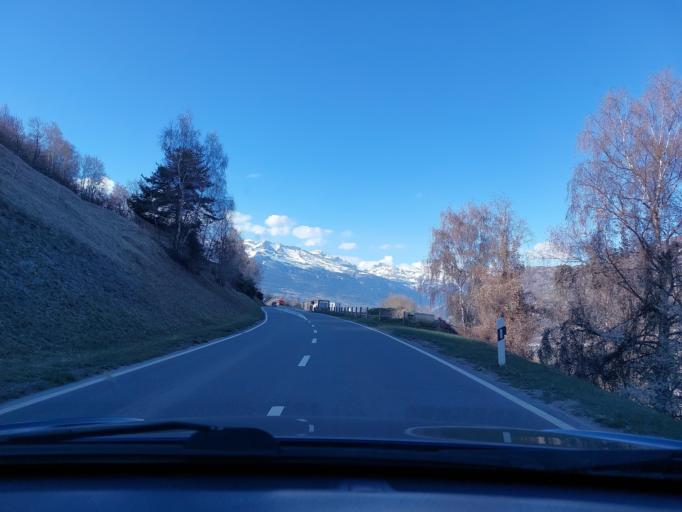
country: CH
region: Valais
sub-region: Herens District
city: Vex
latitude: 46.1983
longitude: 7.4063
